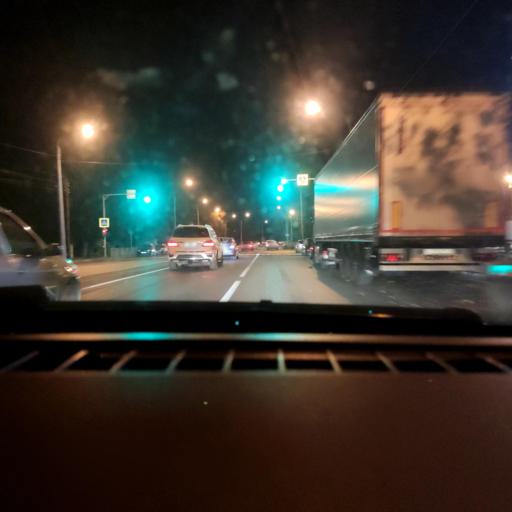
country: RU
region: Voronezj
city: Maslovka
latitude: 51.6038
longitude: 39.2439
